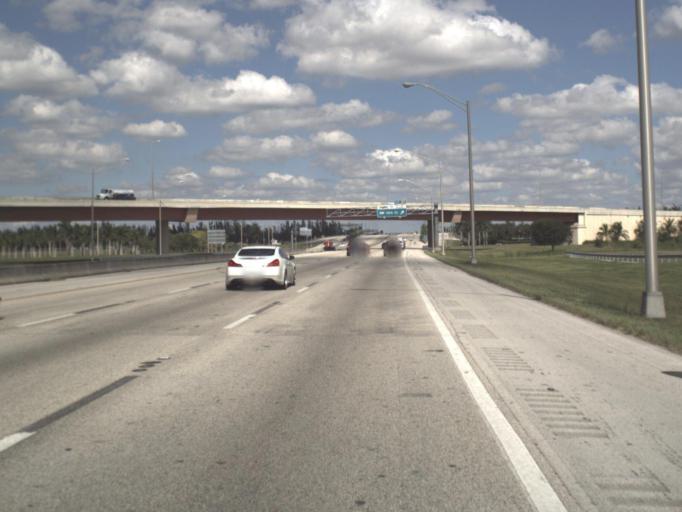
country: US
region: Florida
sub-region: Miami-Dade County
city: Sweetwater
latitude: 25.7744
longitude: -80.3857
